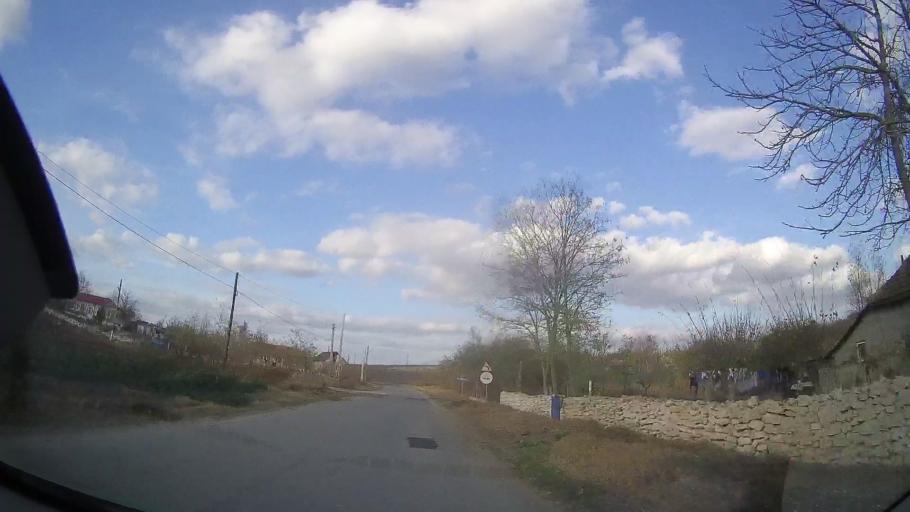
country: RO
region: Constanta
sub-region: Comuna Cerchezu
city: Cerchezu
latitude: 43.8260
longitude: 28.0977
